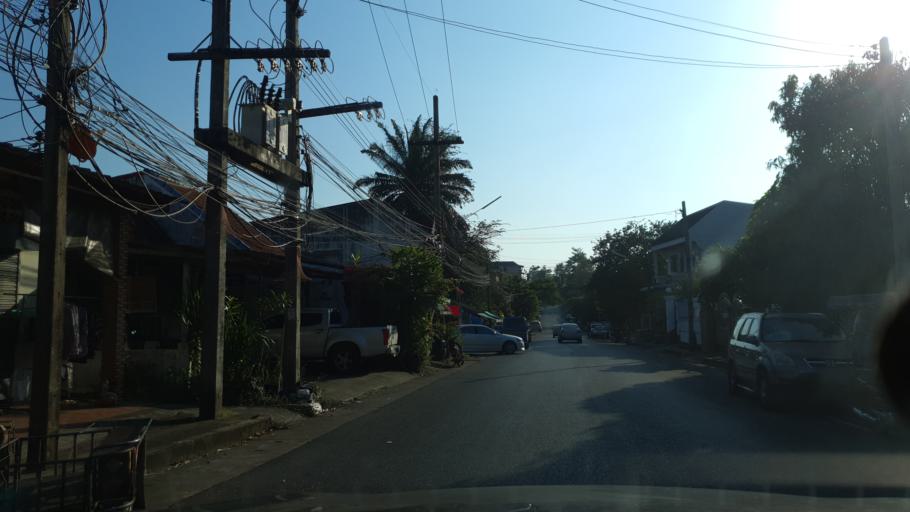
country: TH
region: Krabi
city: Krabi
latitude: 8.0799
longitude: 98.9119
